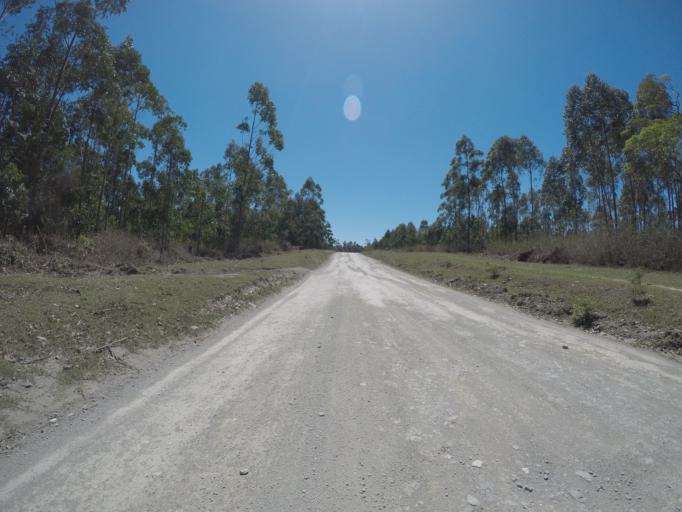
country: ZA
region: Eastern Cape
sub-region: OR Tambo District Municipality
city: Libode
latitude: -31.9554
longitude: 29.0232
